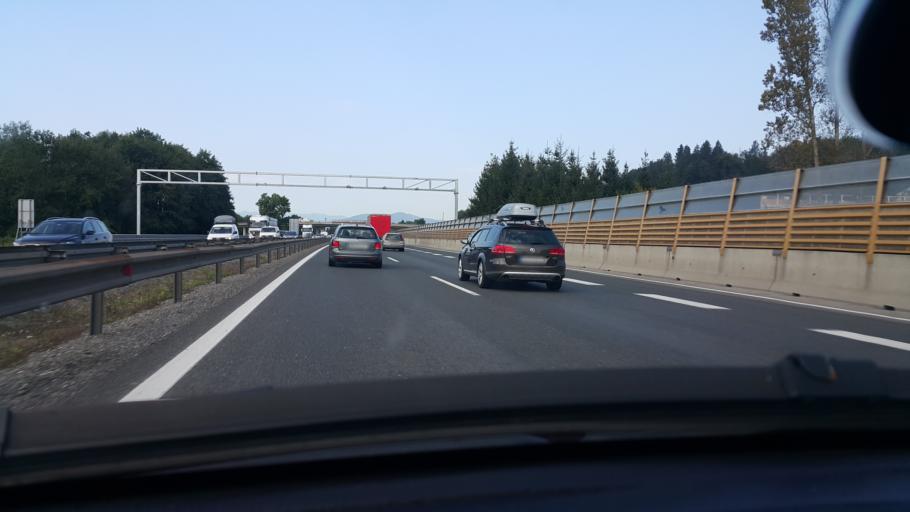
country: SI
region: Brezovica
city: Vnanje Gorice
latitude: 46.0271
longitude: 14.4378
